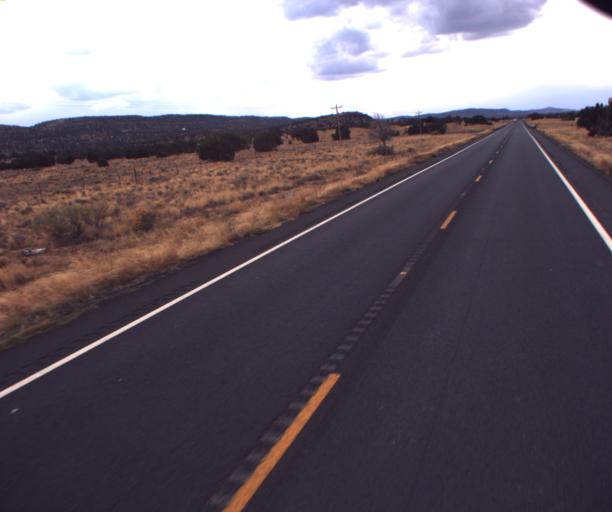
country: US
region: Arizona
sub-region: Coconino County
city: Kaibito
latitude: 36.4833
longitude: -110.6444
